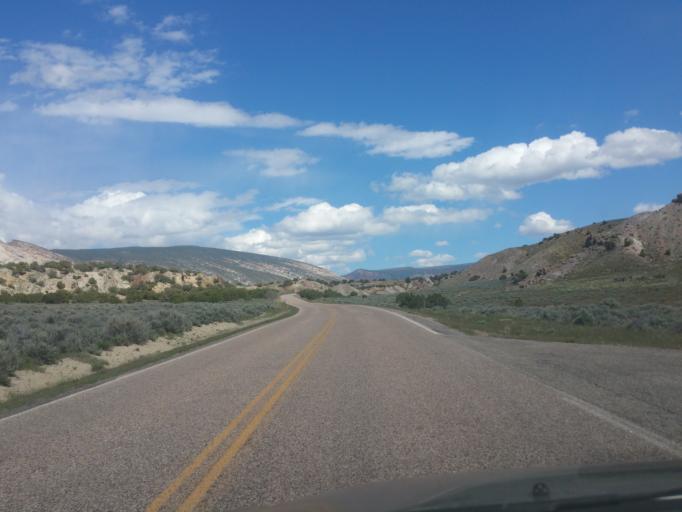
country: US
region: Utah
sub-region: Uintah County
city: Naples
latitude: 40.4372
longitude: -109.2668
